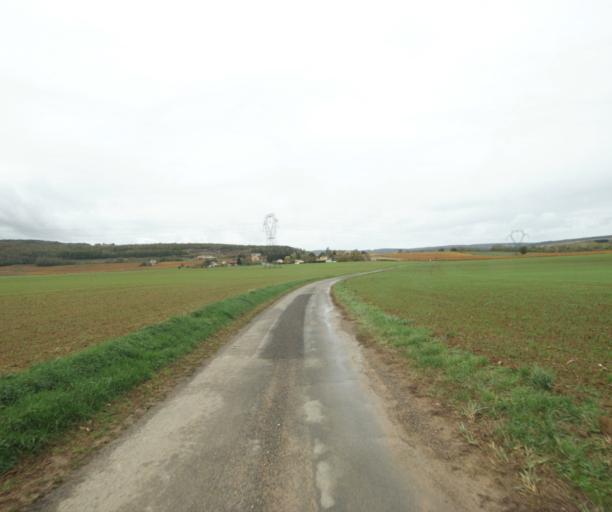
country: FR
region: Bourgogne
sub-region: Departement de Saone-et-Loire
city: Saint-Martin-Belle-Roche
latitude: 46.4680
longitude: 4.8602
